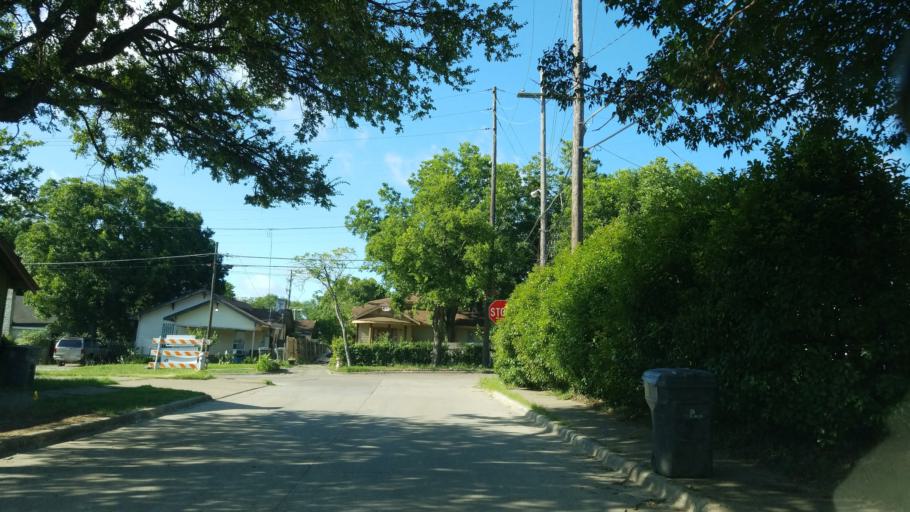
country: US
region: Texas
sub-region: Dallas County
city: Dallas
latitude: 32.7230
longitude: -96.8007
